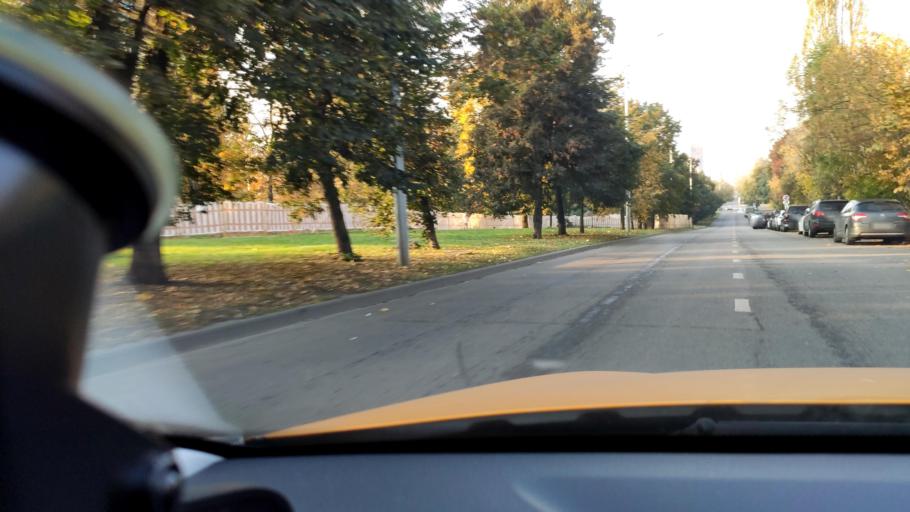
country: RU
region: Moscow
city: Metrogorodok
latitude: 55.8241
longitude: 37.7660
